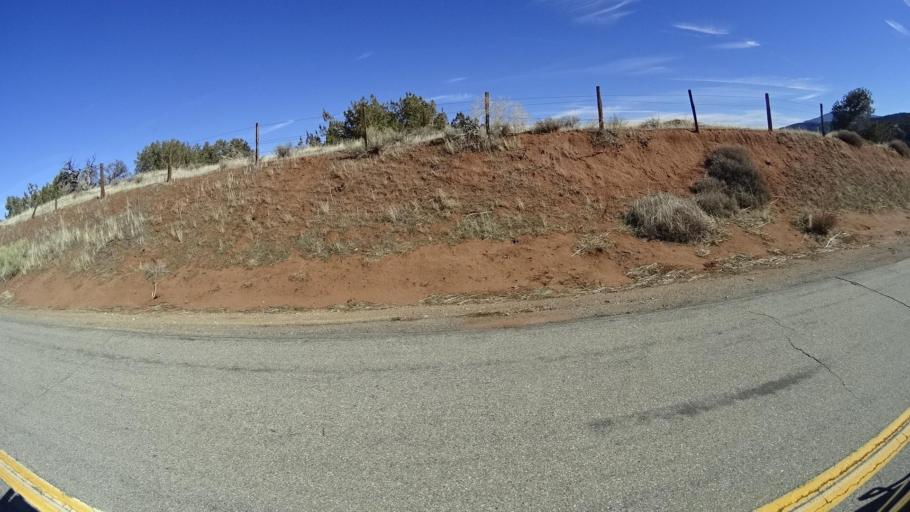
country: US
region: California
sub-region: Kern County
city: Maricopa
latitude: 34.8862
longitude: -119.3544
